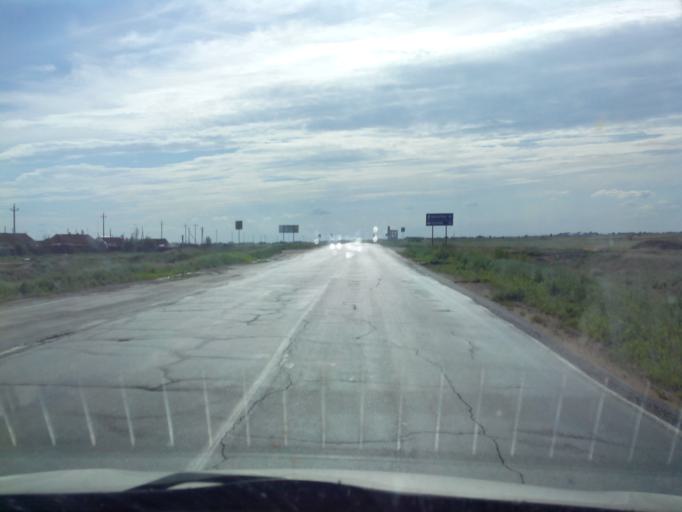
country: RU
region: Astrakhan
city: Znamensk
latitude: 48.5877
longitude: 45.6705
